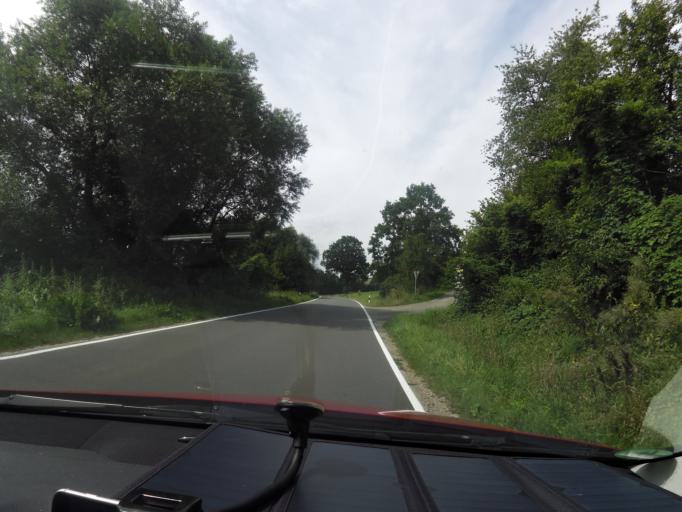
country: DE
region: Thuringia
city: Weissenborn-Luderode
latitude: 51.5615
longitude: 10.3977
